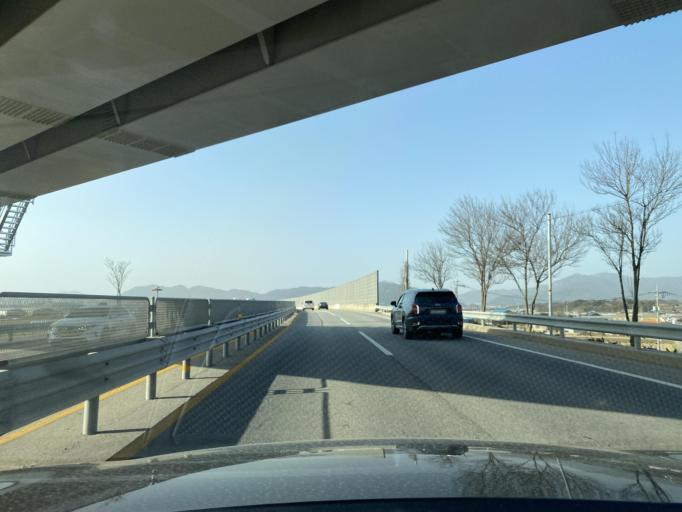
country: KR
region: Chungcheongnam-do
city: Hongsung
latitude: 36.6919
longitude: 126.7246
